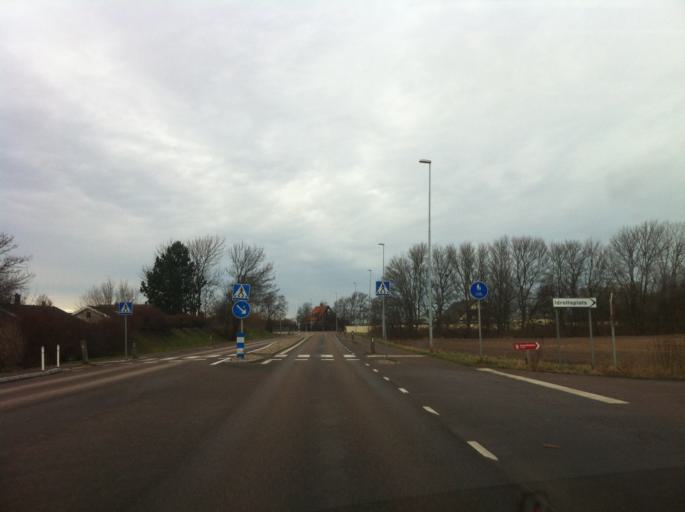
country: SE
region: Skane
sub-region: Hoganas Kommun
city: Hoganas
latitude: 56.1409
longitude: 12.5871
